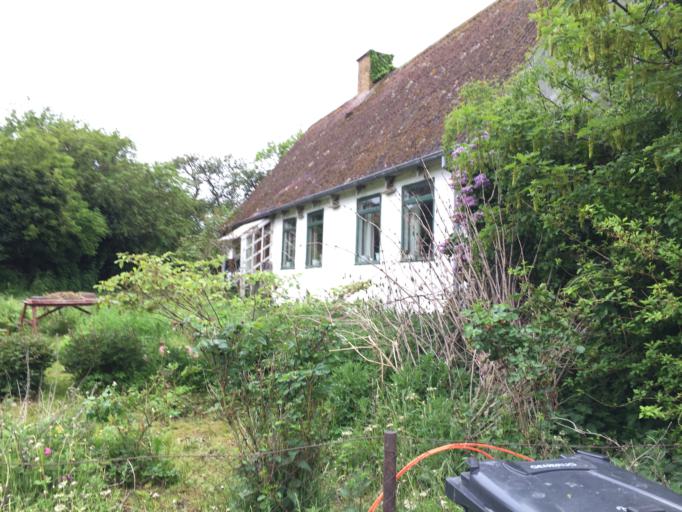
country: DK
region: Zealand
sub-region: Vordingborg Kommune
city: Stege
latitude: 55.0420
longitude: 12.1950
